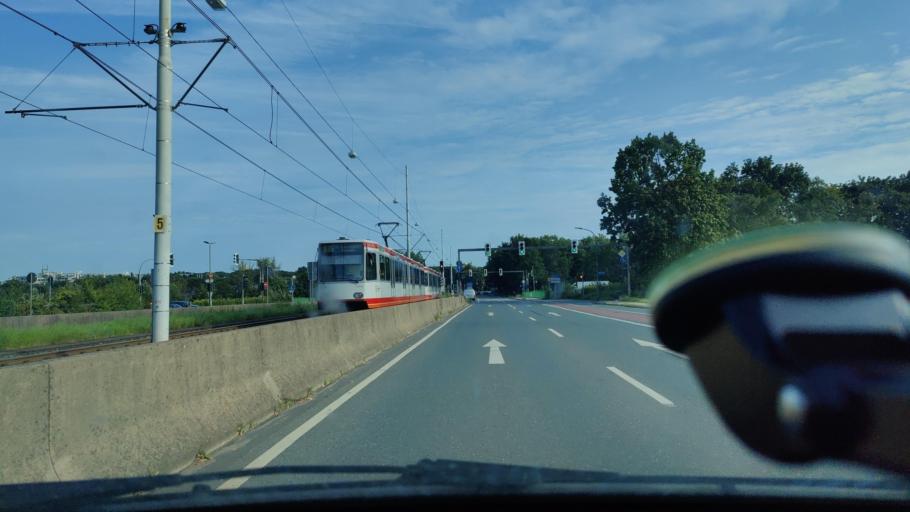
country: DE
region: North Rhine-Westphalia
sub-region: Regierungsbezirk Arnsberg
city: Bochum
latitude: 51.4604
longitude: 7.2356
